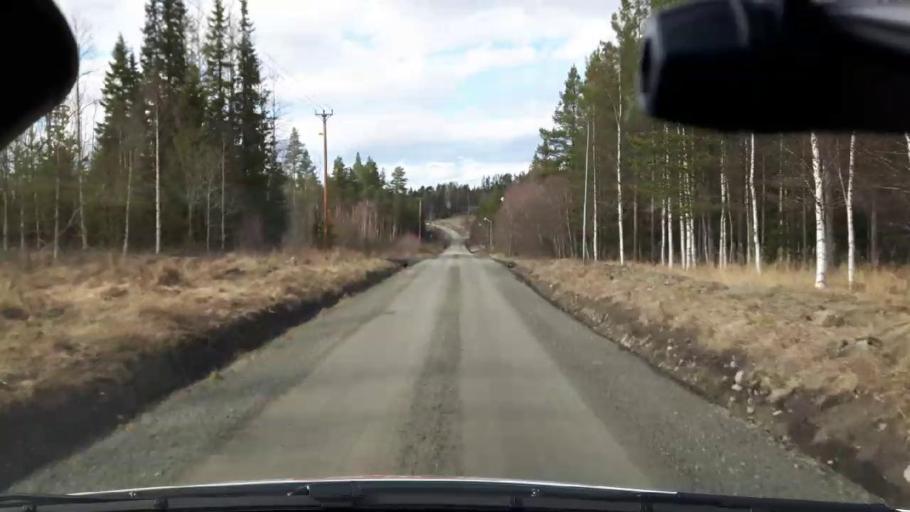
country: SE
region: Jaemtland
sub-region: Bergs Kommun
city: Hoverberg
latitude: 62.8773
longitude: 14.6666
